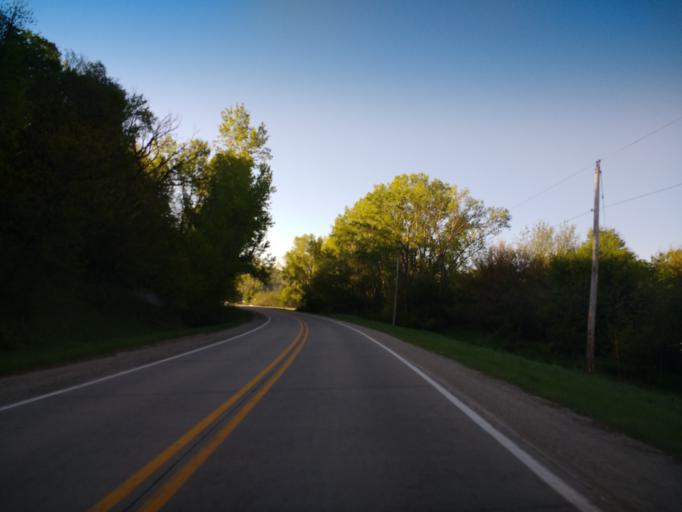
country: US
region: Iowa
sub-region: Harrison County
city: Missouri Valley
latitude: 41.4355
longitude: -95.8691
